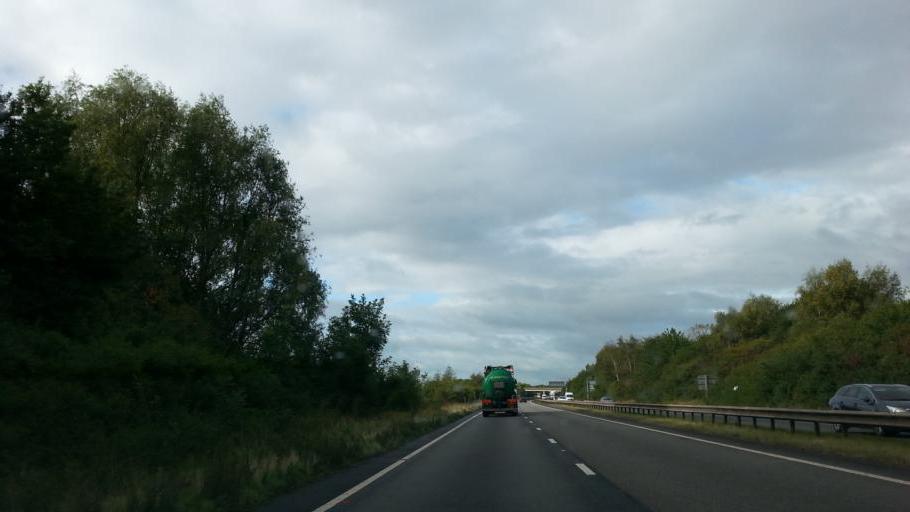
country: GB
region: England
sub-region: Leicestershire
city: Ashby de la Zouch
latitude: 52.7404
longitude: -1.4587
